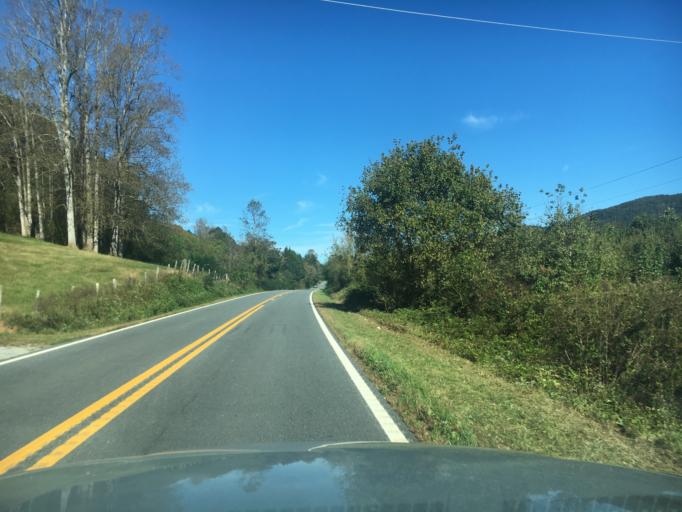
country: US
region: North Carolina
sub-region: Rutherford County
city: Spindale
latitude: 35.5293
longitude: -81.8562
